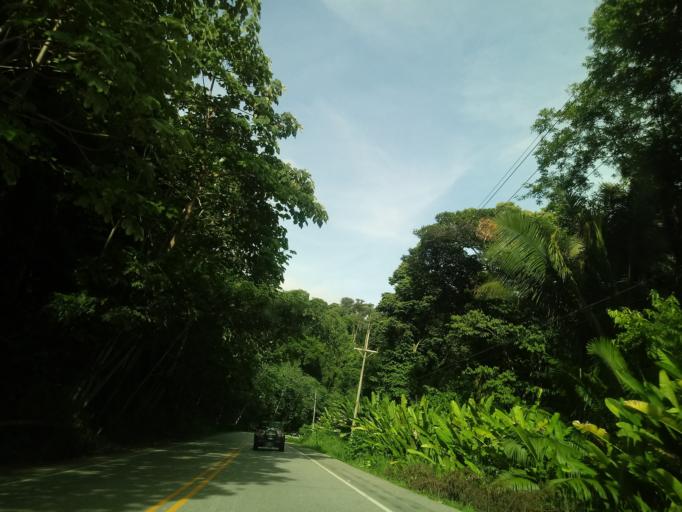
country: CR
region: San Jose
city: Daniel Flores
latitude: 9.1907
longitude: -83.7749
